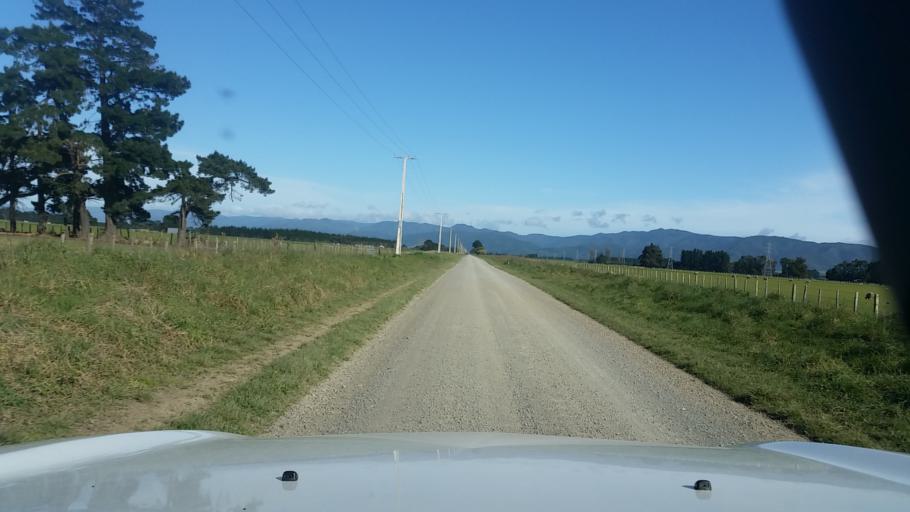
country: NZ
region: Wellington
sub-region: Masterton District
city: Masterton
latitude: -41.1191
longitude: 175.4276
